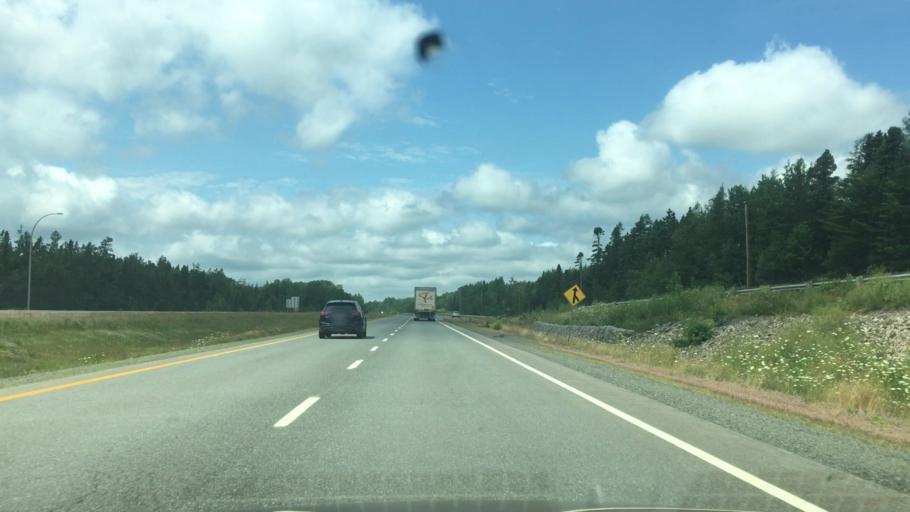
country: CA
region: Nova Scotia
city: Oxford
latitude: 45.7228
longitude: -63.8827
